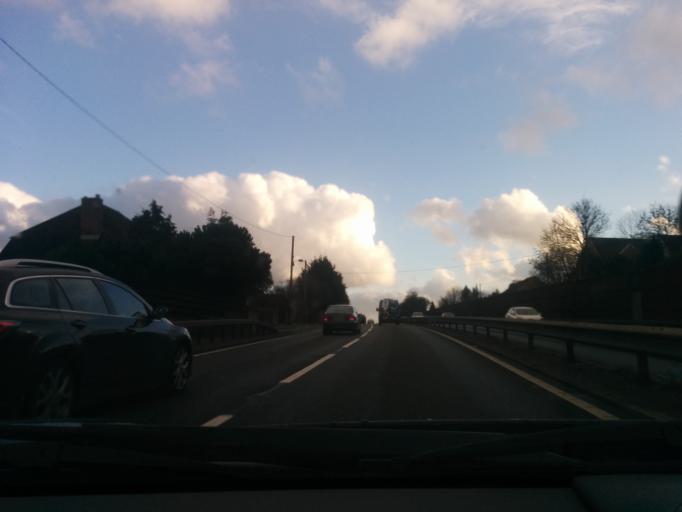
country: GB
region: England
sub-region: Oxfordshire
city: Boars Hill
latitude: 51.7489
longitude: -1.2931
